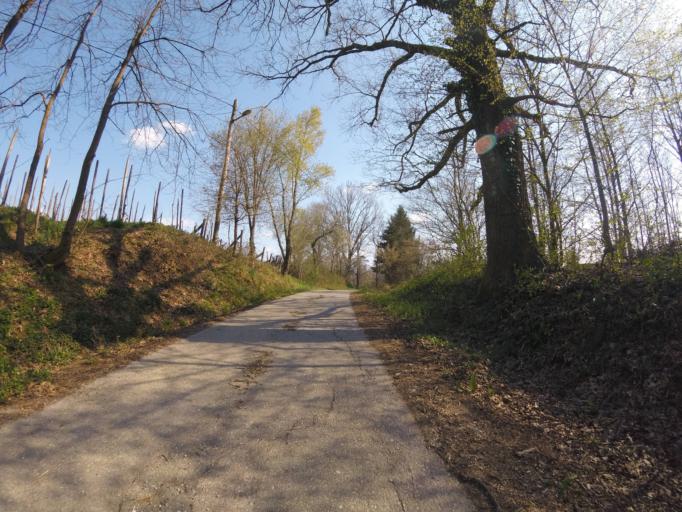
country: HR
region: Sisacko-Moslavacka
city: Gvozd
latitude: 45.5146
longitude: 15.9217
